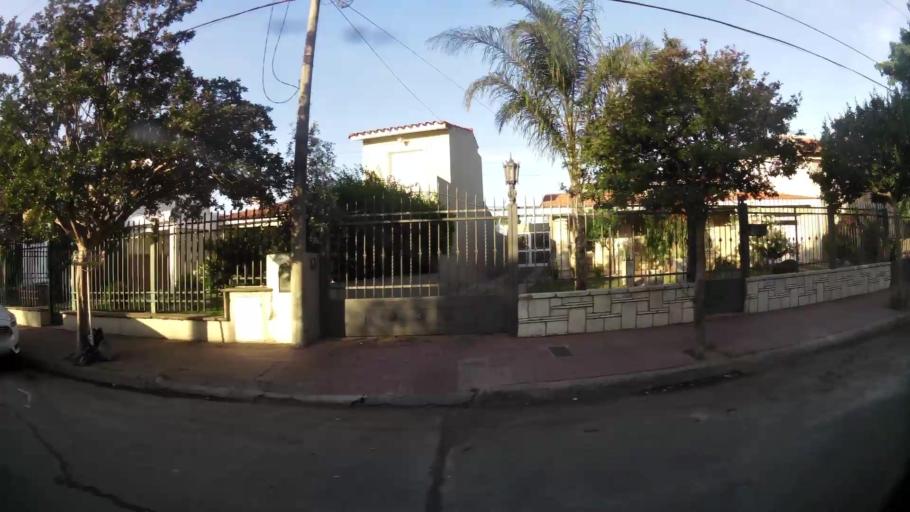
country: AR
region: Cordoba
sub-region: Departamento de Capital
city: Cordoba
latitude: -31.3802
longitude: -64.2260
